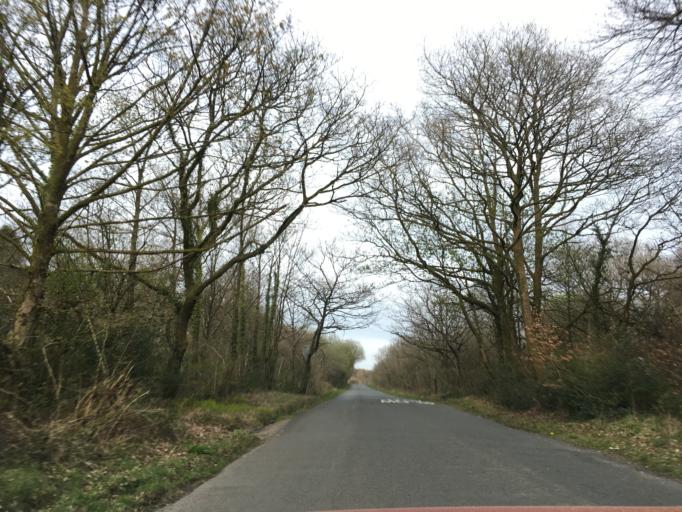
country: GB
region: Wales
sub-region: Caerphilly County Borough
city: Caerphilly
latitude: 51.5583
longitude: -3.2319
